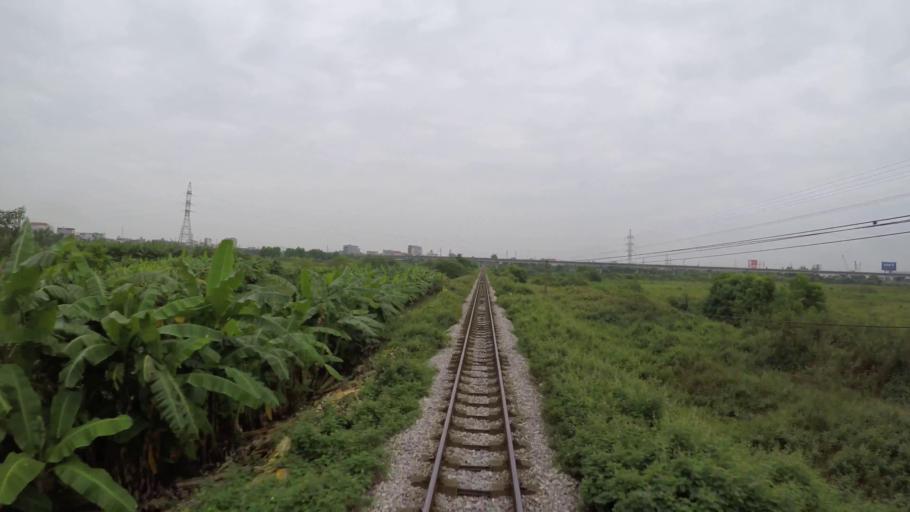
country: VN
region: Hai Phong
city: An Duong
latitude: 20.9106
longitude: 106.5701
